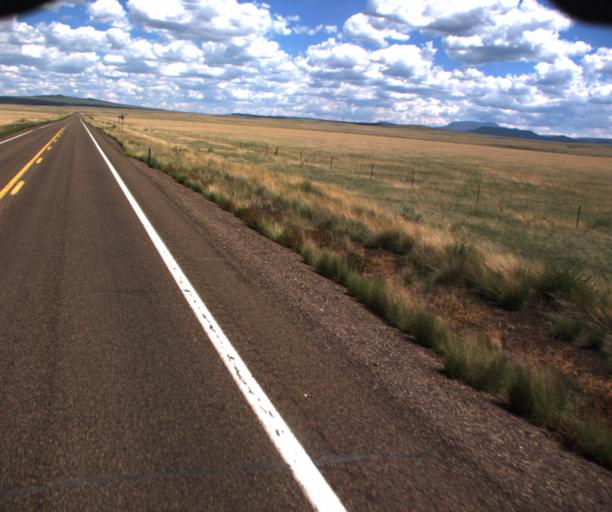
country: US
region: Arizona
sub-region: Apache County
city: Springerville
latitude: 34.1929
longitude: -109.3634
